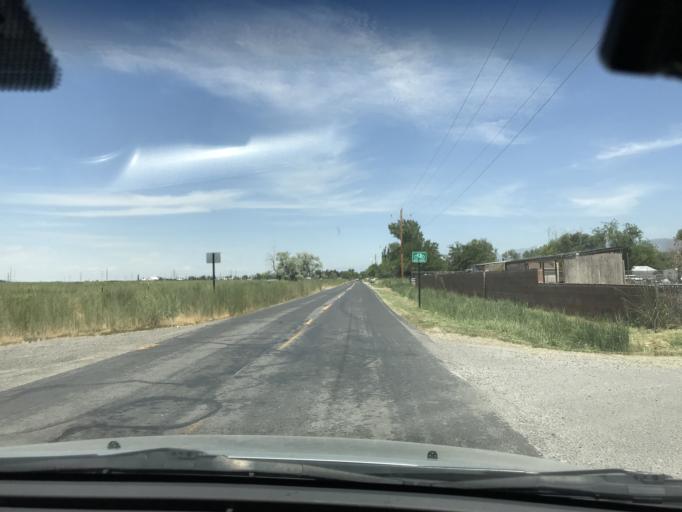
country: US
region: Utah
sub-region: Davis County
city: North Salt Lake
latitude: 40.8268
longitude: -111.9535
